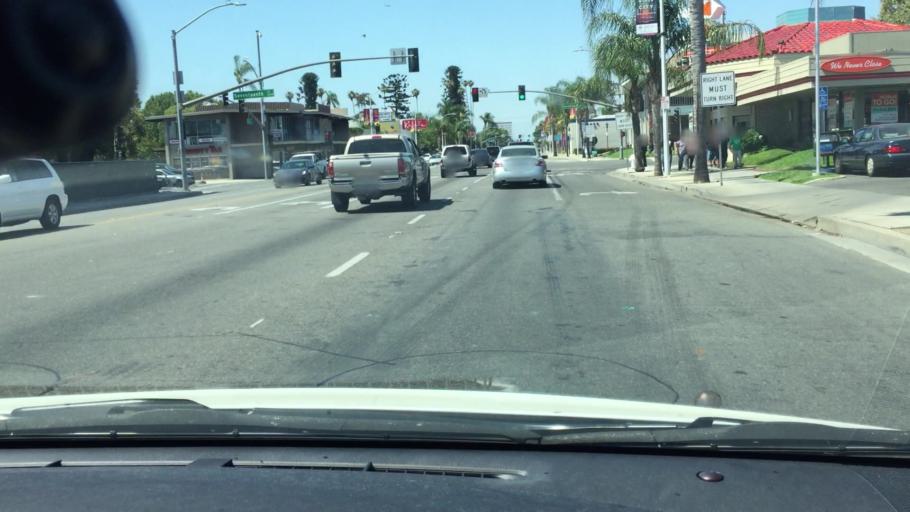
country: US
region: California
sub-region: Orange County
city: Santa Ana
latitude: 33.7595
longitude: -117.8675
